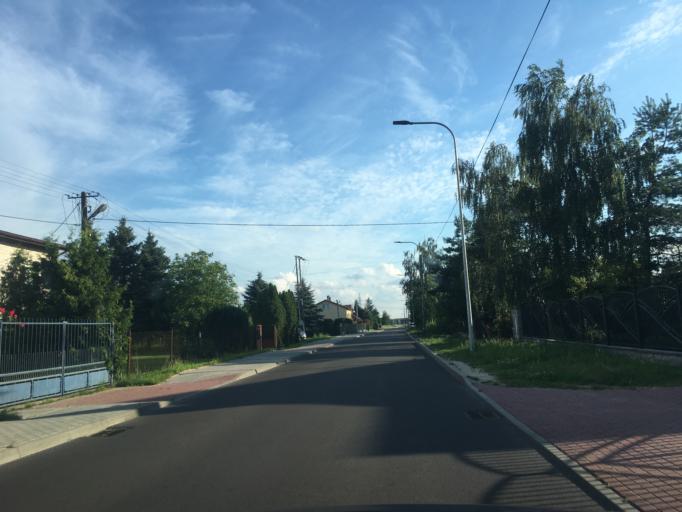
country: PL
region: Masovian Voivodeship
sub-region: Powiat wolominski
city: Radzymin
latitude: 52.4031
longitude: 21.2072
